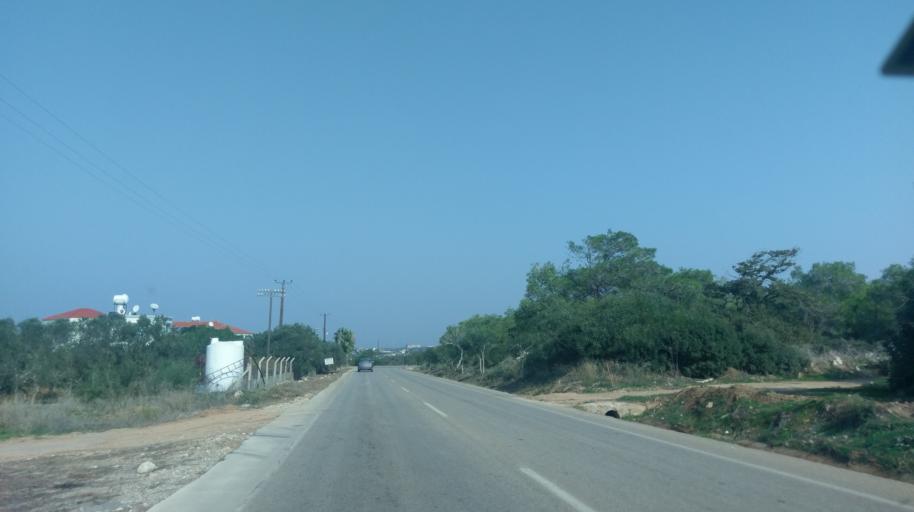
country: CY
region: Ammochostos
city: Leonarisso
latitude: 35.4875
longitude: 34.1520
